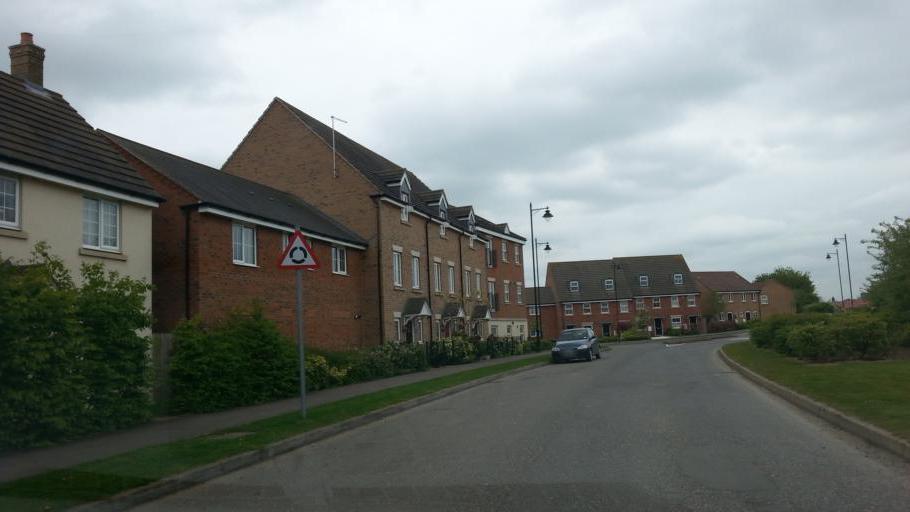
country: GB
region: England
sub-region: Lincolnshire
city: Bourne
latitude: 52.7585
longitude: -0.3782
